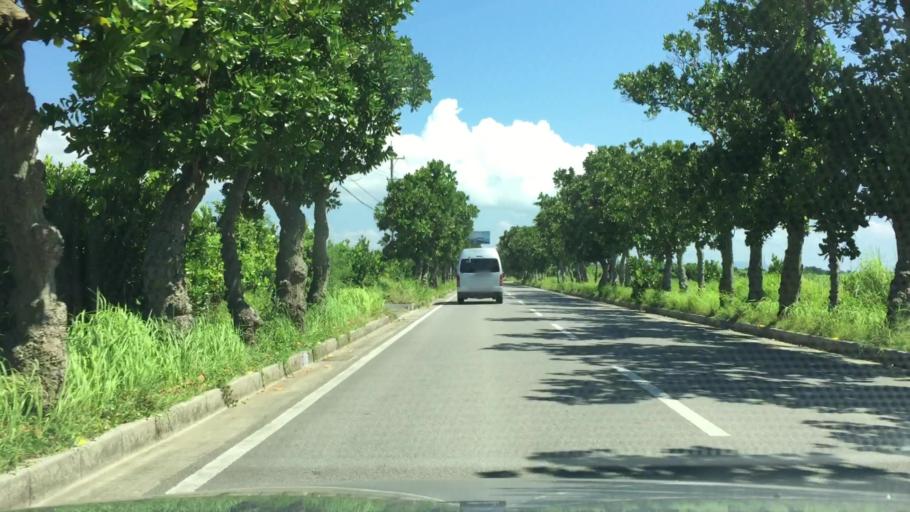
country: JP
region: Okinawa
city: Ishigaki
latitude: 24.3727
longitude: 124.2462
